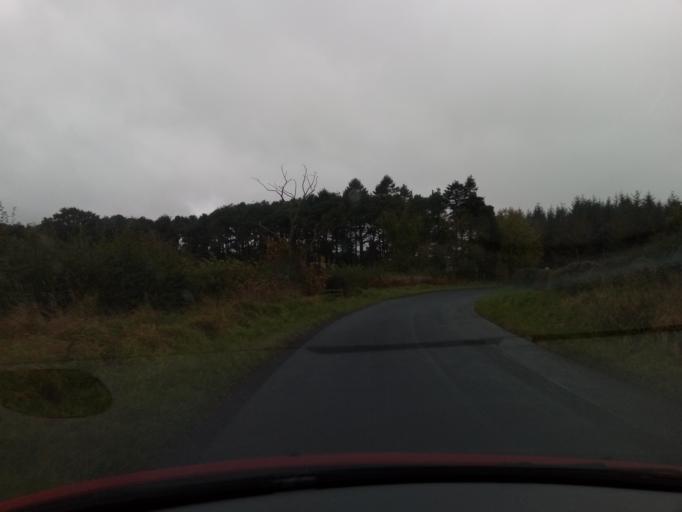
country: GB
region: Scotland
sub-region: The Scottish Borders
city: Melrose
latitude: 55.5116
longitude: -2.7499
